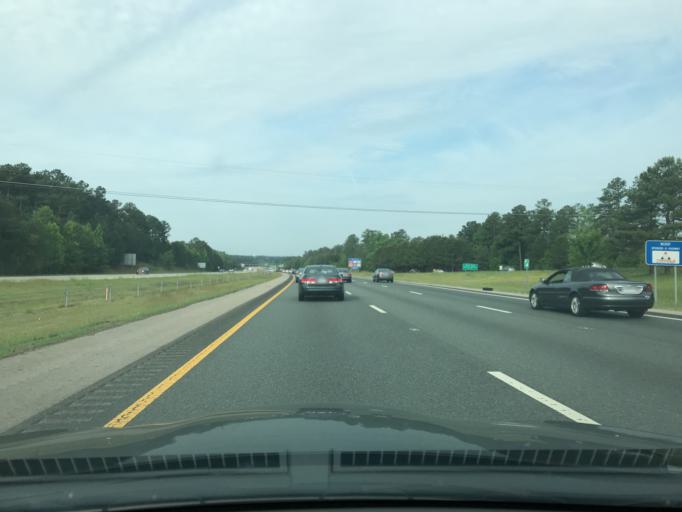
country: US
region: North Carolina
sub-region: Wake County
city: Morrisville
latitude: 35.9040
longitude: -78.7750
